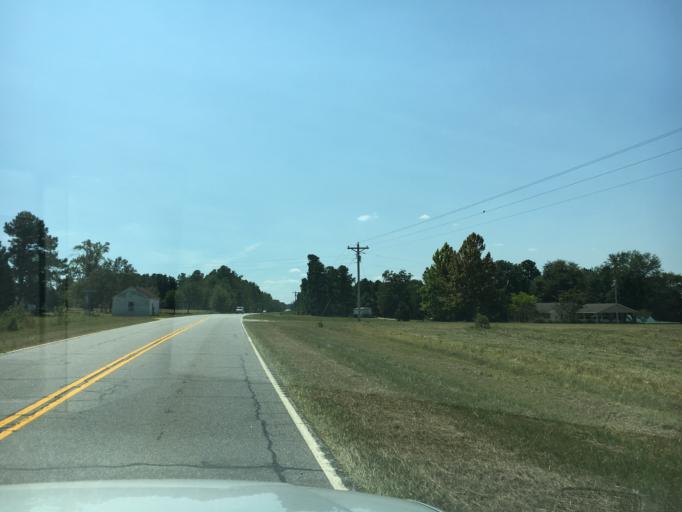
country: US
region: South Carolina
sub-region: Lexington County
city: Batesburg
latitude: 33.7729
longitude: -81.6406
